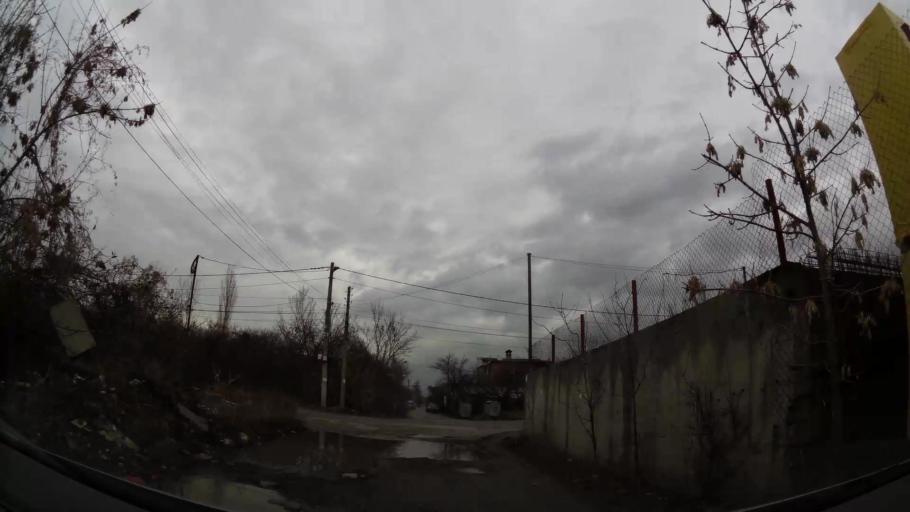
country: BG
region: Sofia-Capital
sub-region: Stolichna Obshtina
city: Sofia
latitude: 42.7219
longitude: 23.2796
